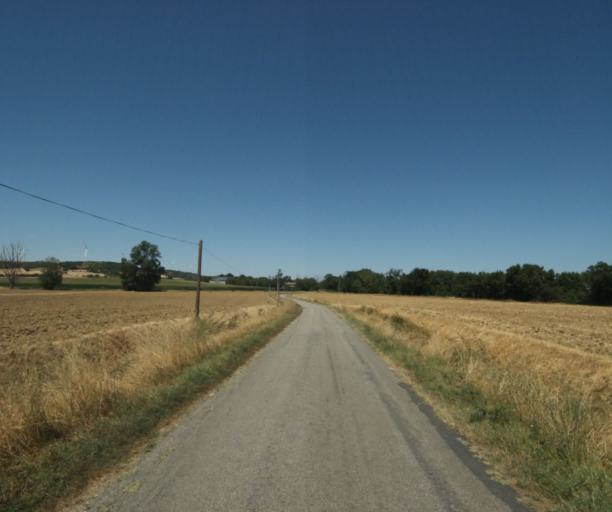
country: FR
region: Midi-Pyrenees
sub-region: Departement de la Haute-Garonne
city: Saint-Felix-Lauragais
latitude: 43.4524
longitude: 1.9366
